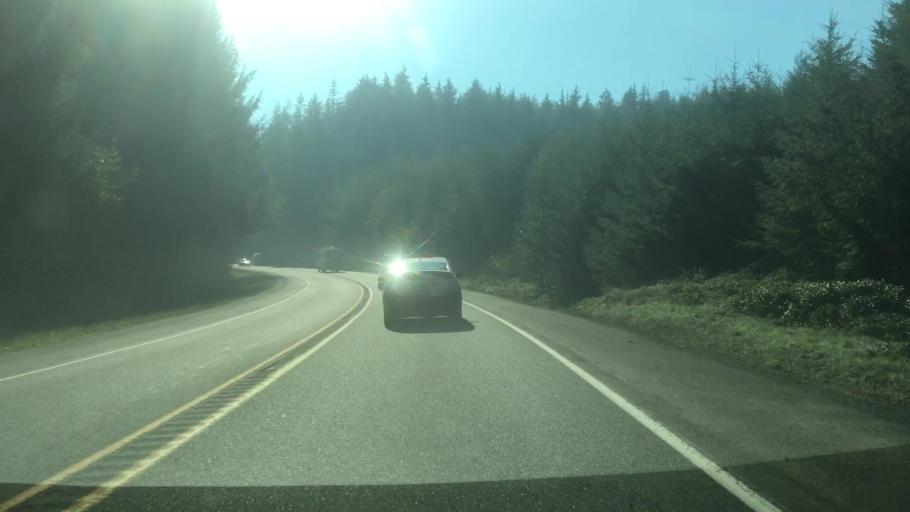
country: US
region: Washington
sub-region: Grays Harbor County
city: Central Park
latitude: 46.9278
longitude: -123.7154
